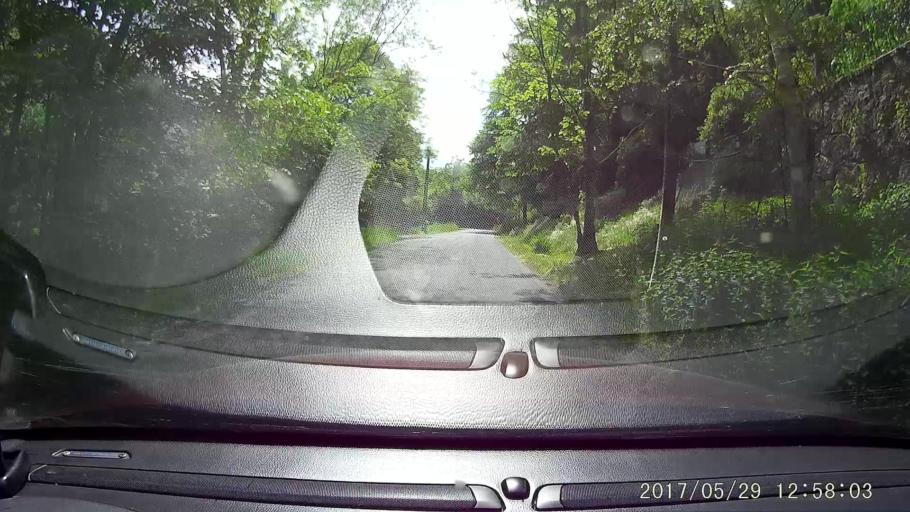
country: PL
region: Lower Silesian Voivodeship
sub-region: Jelenia Gora
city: Jelenia Gora
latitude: 50.9252
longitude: 15.6751
